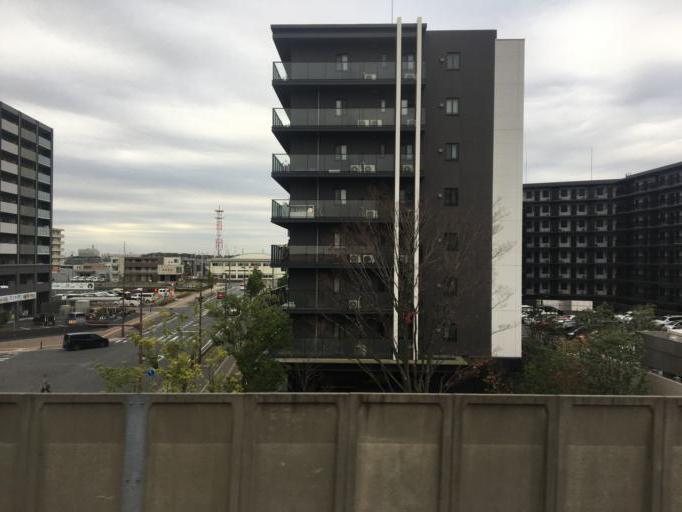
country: JP
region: Saitama
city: Yoshikawa
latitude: 35.8762
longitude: 139.8205
